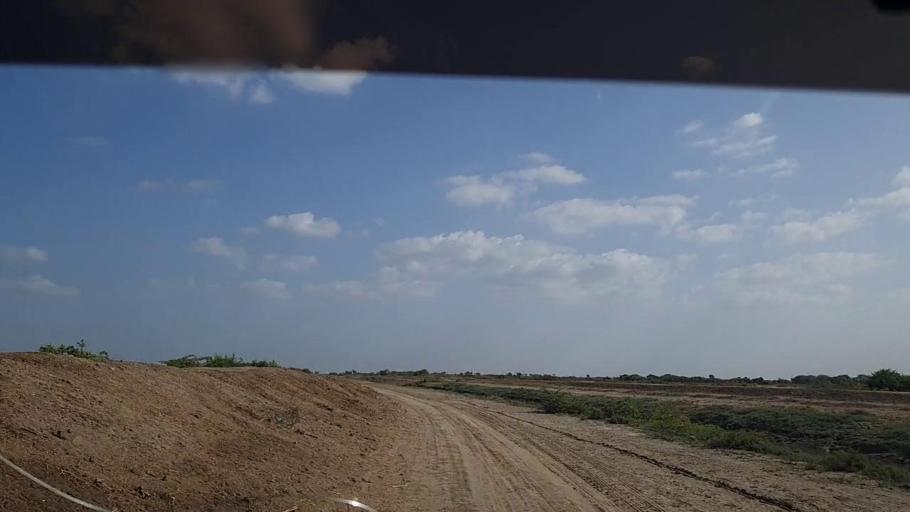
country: PK
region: Sindh
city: Kadhan
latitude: 24.4525
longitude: 68.8581
